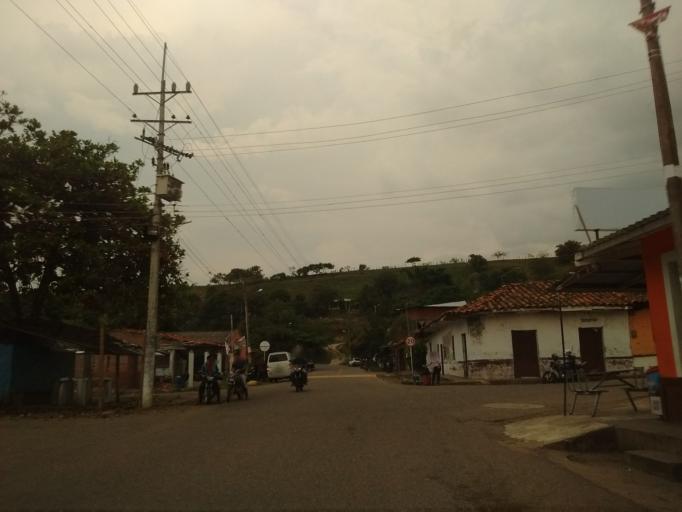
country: CO
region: Cauca
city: Caloto
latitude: 3.0657
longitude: -76.3539
